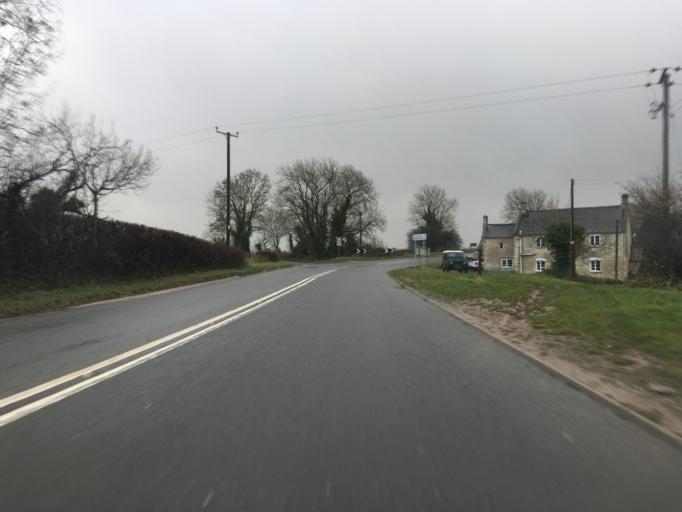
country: GB
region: England
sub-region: South Gloucestershire
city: Horton
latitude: 51.5276
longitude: -2.3421
